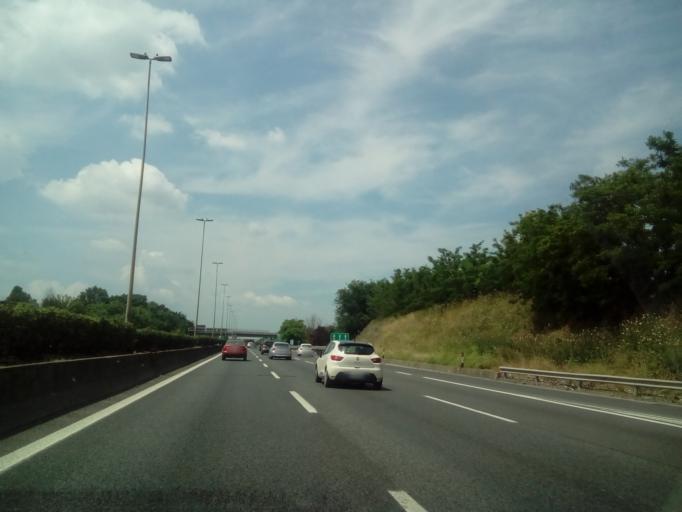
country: IT
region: Latium
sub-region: Citta metropolitana di Roma Capitale
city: Colle Verde
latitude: 41.9466
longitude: 12.5909
